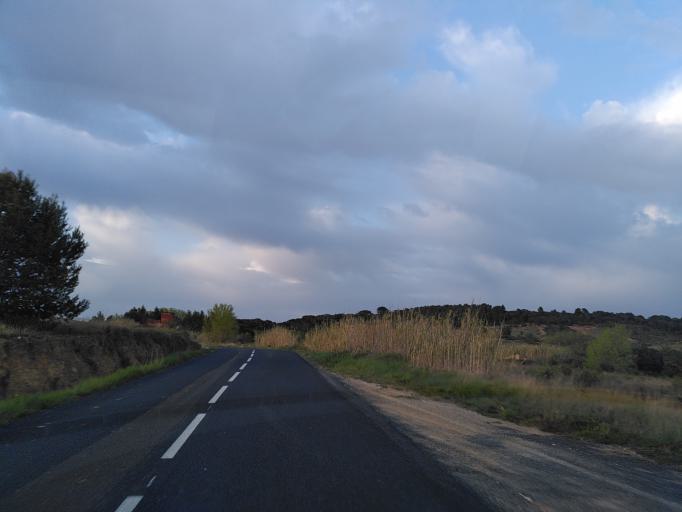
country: FR
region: Languedoc-Roussillon
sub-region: Departement des Pyrenees-Orientales
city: Estagel
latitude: 42.8032
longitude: 2.6982
